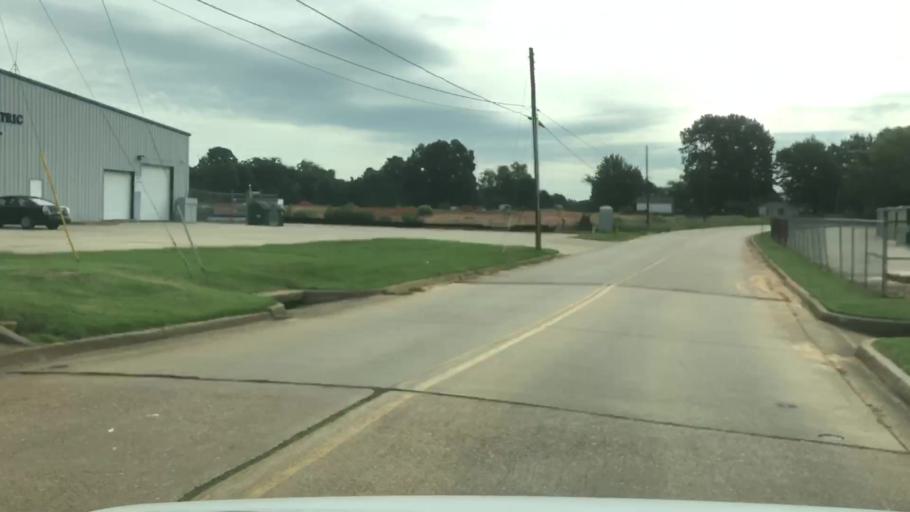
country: US
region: Texas
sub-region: Bowie County
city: Wake Village
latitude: 33.4433
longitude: -94.0930
